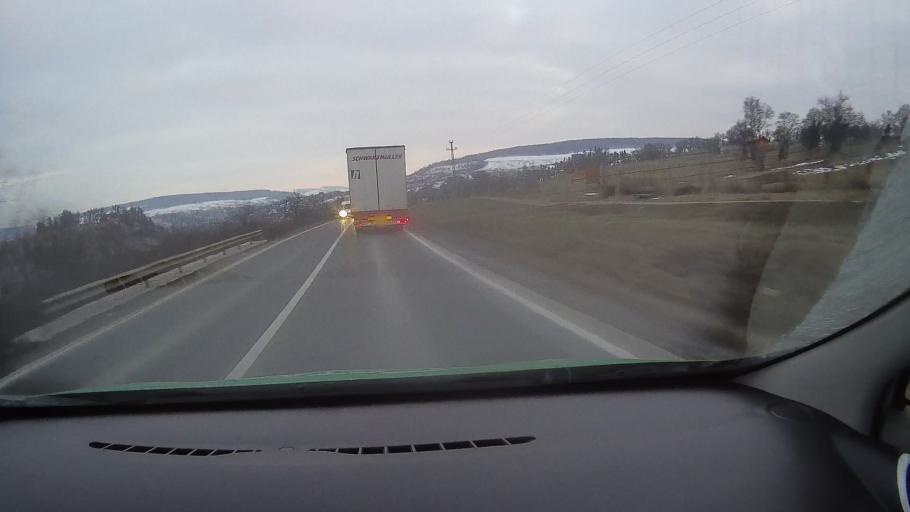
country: RO
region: Harghita
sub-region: Municipiul Odorheiu Secuiesc
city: Odorheiu Secuiesc
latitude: 46.3230
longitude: 25.2801
